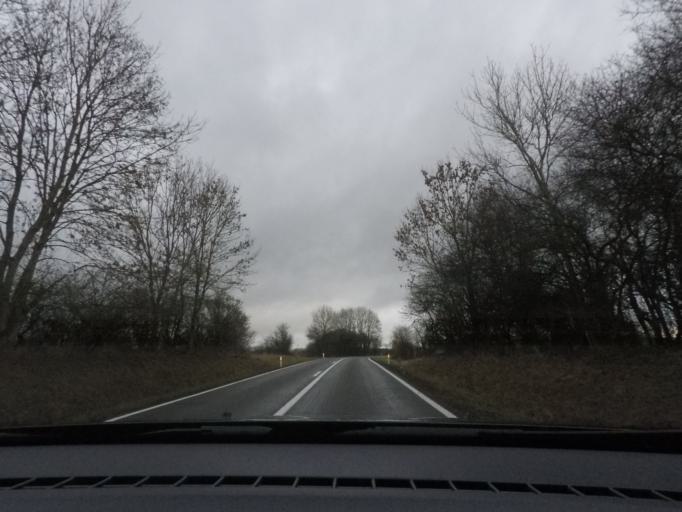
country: BE
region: Wallonia
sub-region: Province du Luxembourg
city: Tintigny
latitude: 49.6991
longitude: 5.5279
